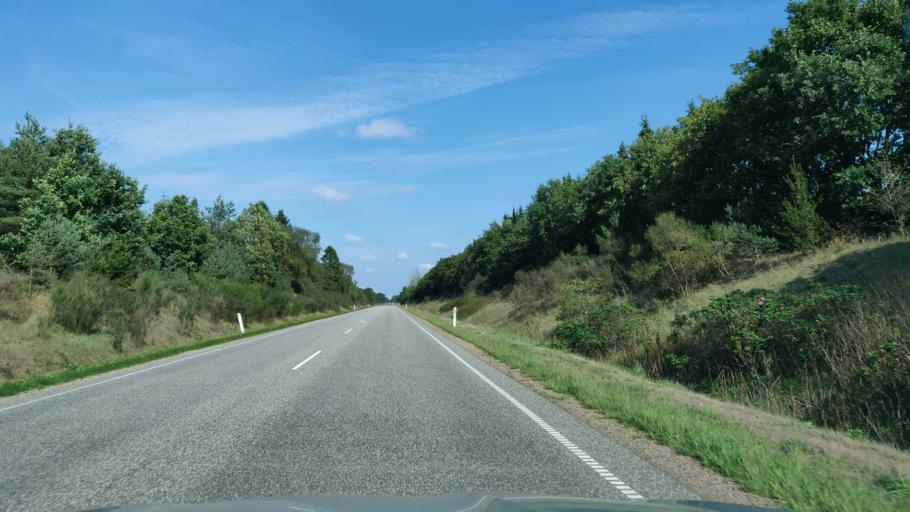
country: DK
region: Central Jutland
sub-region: Herning Kommune
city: Sunds
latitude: 56.3704
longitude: 8.9819
